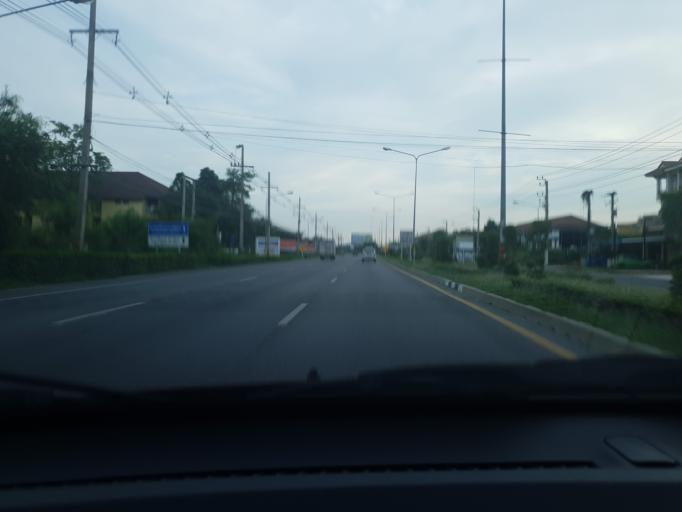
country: TH
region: Prachuap Khiri Khan
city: Hua Hin
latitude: 12.6389
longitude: 99.9487
